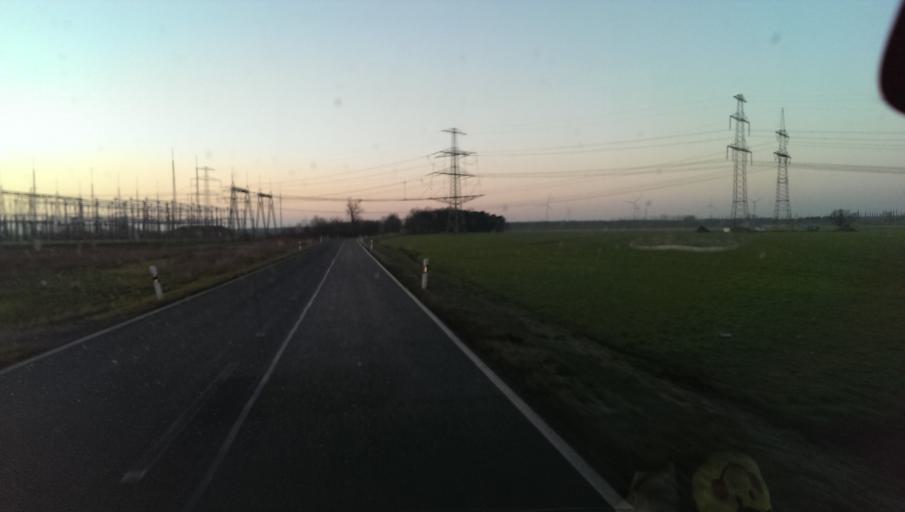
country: DE
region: Saxony-Anhalt
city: Holzdorf
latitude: 51.8275
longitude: 13.1620
